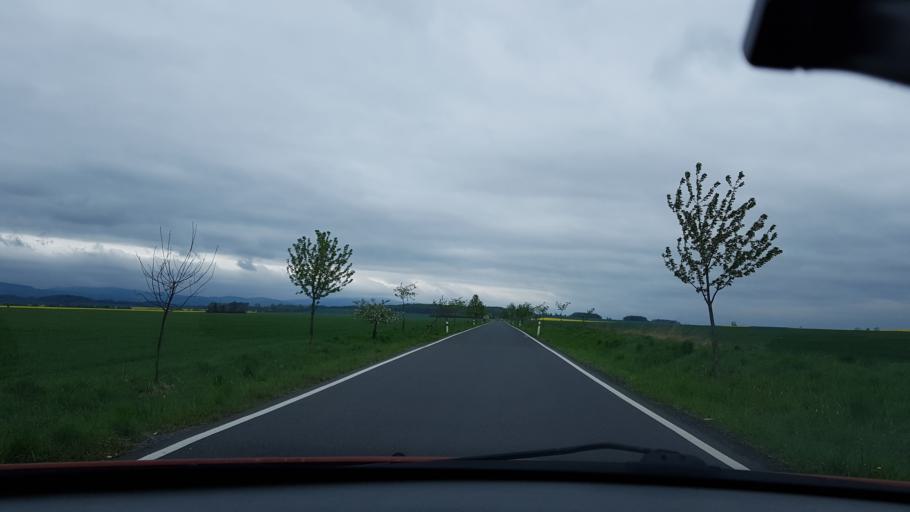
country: CZ
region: Olomoucky
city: Vidnava
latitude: 50.3772
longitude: 17.1730
